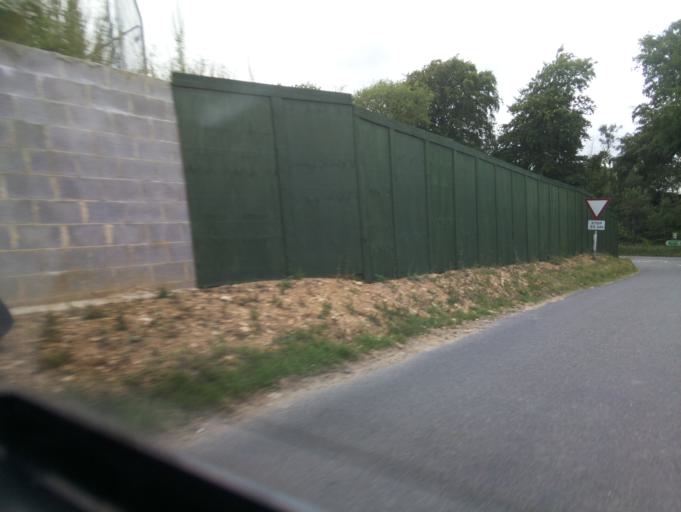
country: GB
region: England
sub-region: Gloucestershire
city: Moreton in Marsh
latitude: 51.9919
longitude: -1.7527
